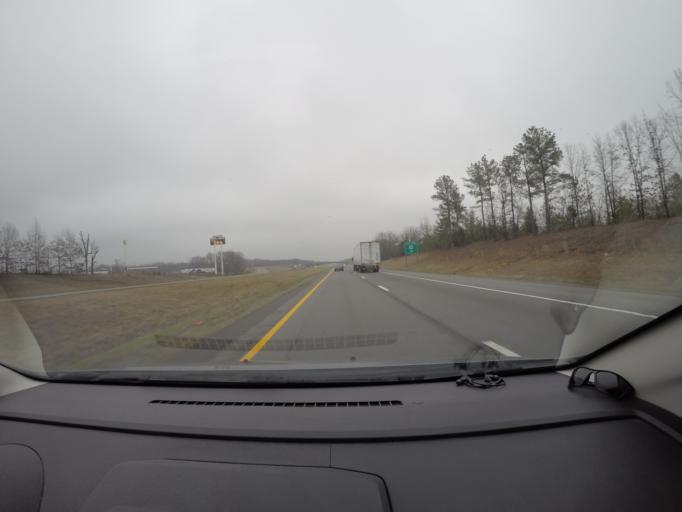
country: US
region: Tennessee
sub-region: Coffee County
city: New Union
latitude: 35.5375
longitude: -86.1690
